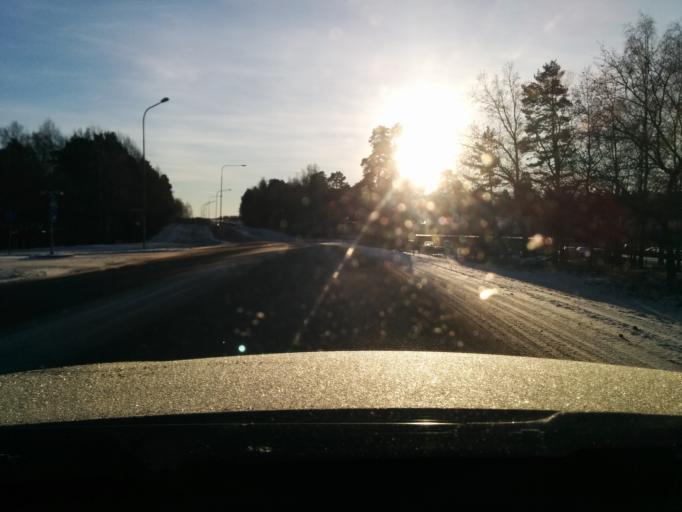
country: SE
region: Vaestmanland
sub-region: Vasteras
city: Vasteras
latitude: 59.6208
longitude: 16.5997
